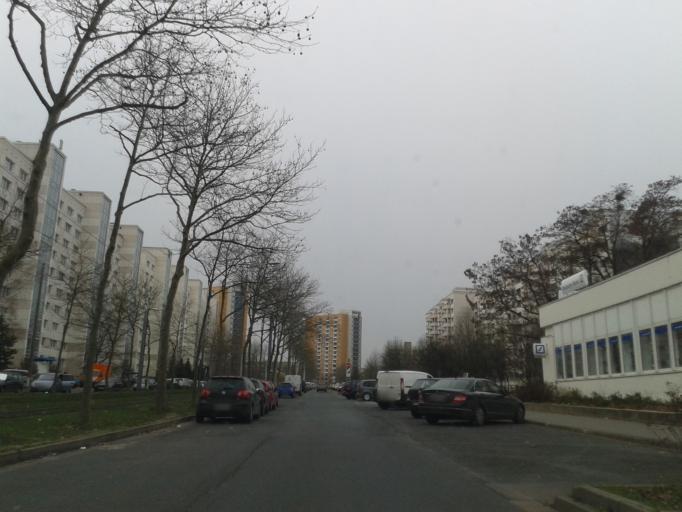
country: DE
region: Saxony
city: Heidenau
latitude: 51.0074
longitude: 13.8019
